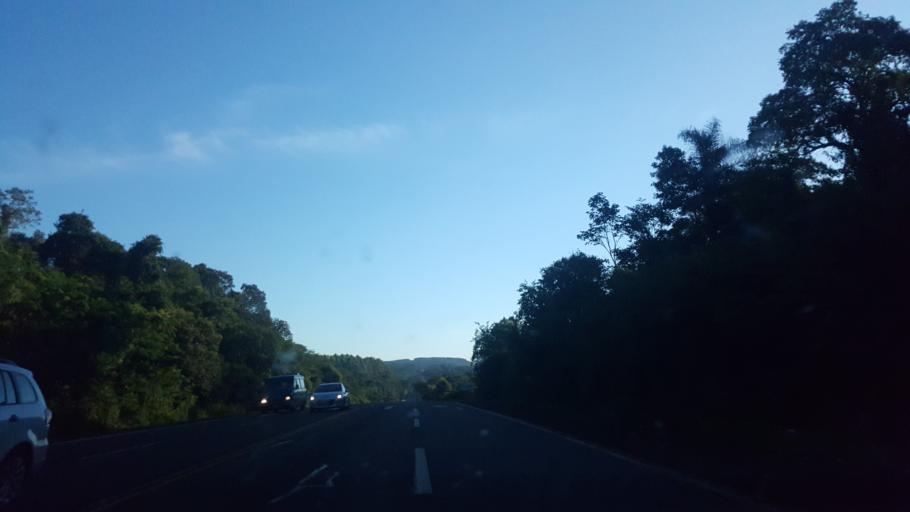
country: AR
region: Misiones
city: El Alcazar
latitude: -26.6975
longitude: -54.8355
